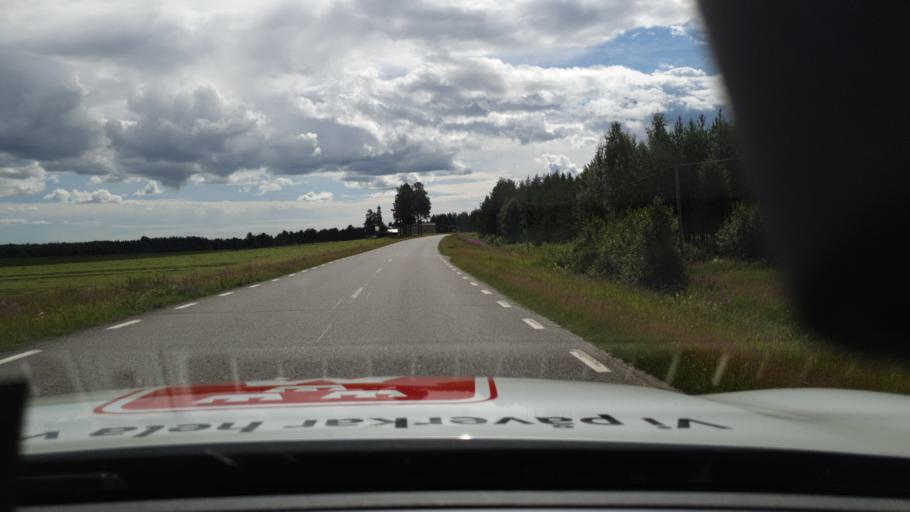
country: SE
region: Norrbotten
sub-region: Bodens Kommun
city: Boden
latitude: 65.8973
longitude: 21.6752
